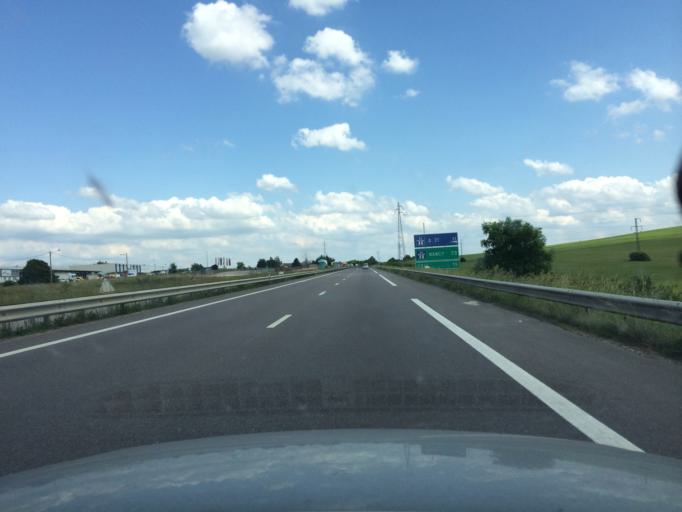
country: FR
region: Lorraine
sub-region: Departement de Meurthe-et-Moselle
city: Foug
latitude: 48.6829
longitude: 5.7356
